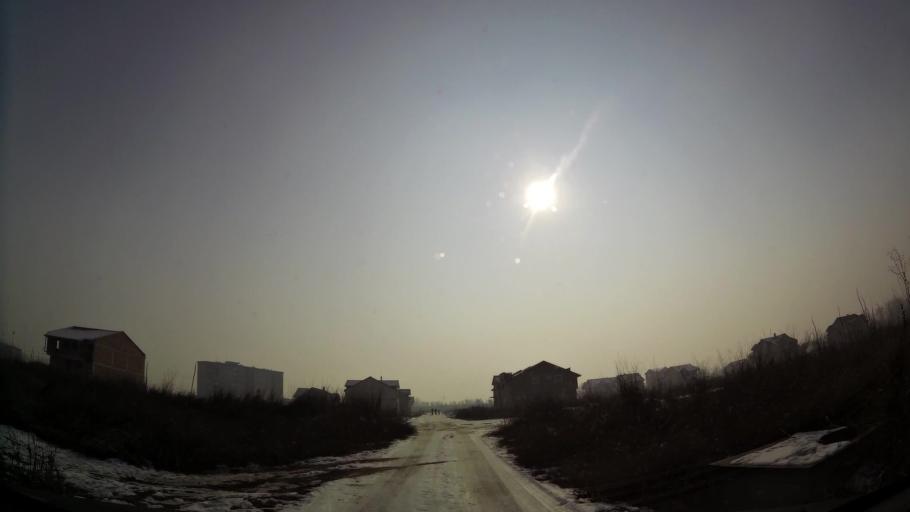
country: MK
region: Kisela Voda
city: Kisela Voda
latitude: 41.9940
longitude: 21.5171
